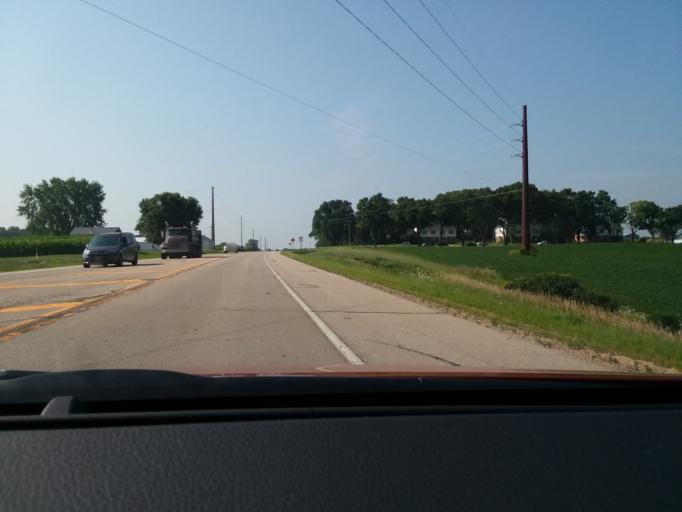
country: US
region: Wisconsin
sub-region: Dane County
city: Waunakee
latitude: 43.1853
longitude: -89.4117
